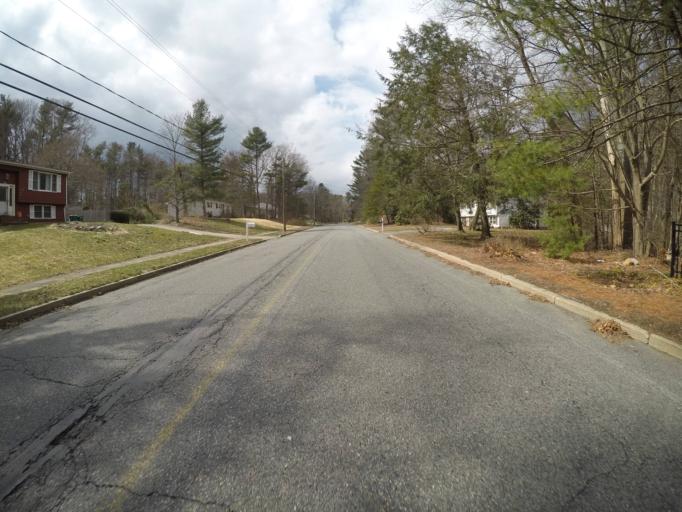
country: US
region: Massachusetts
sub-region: Bristol County
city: Easton
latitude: 42.0364
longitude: -71.1119
